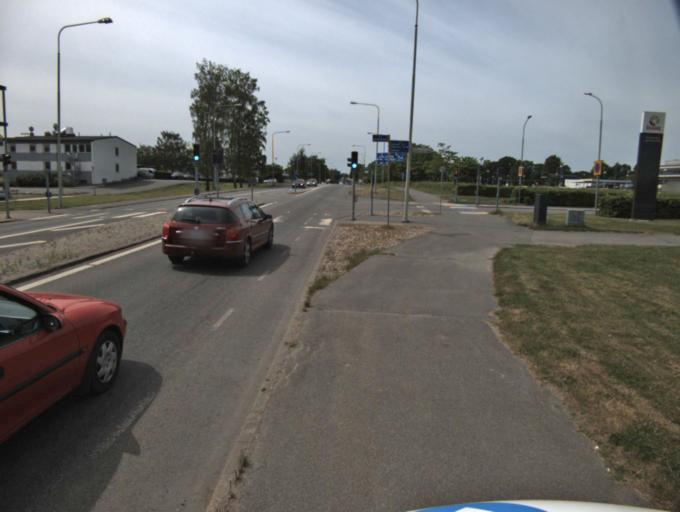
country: SE
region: Skane
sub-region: Kristianstads Kommun
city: Kristianstad
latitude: 56.0296
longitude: 14.1772
